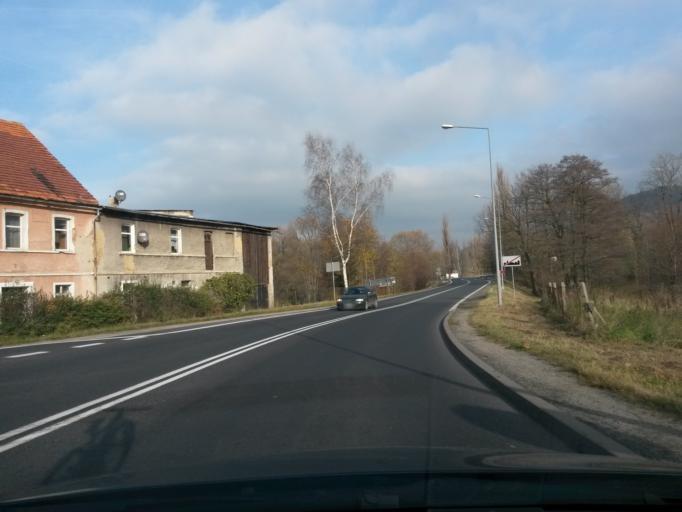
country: PL
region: Lower Silesian Voivodeship
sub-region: Powiat jeleniogorski
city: Janowice Wielkie
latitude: 50.9143
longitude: 15.9579
